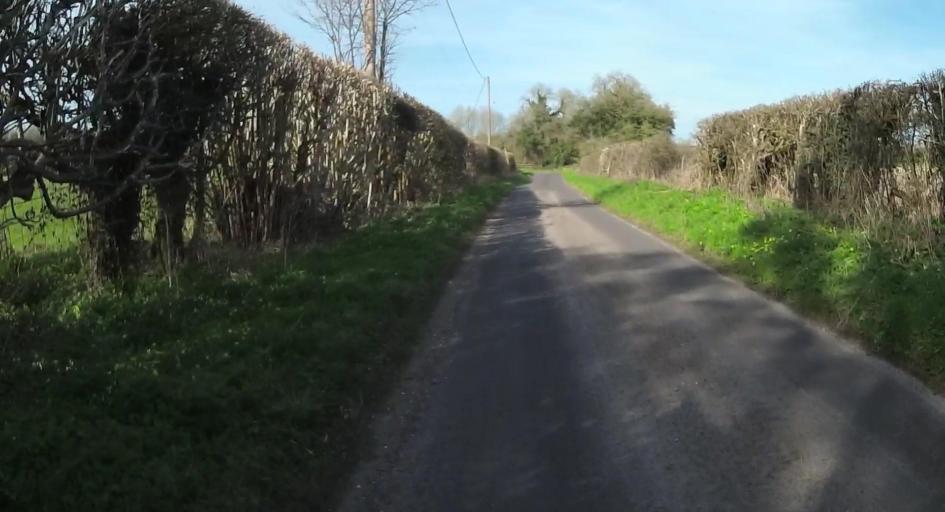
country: GB
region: England
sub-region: Hampshire
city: Highclere
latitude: 51.2667
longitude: -1.3773
